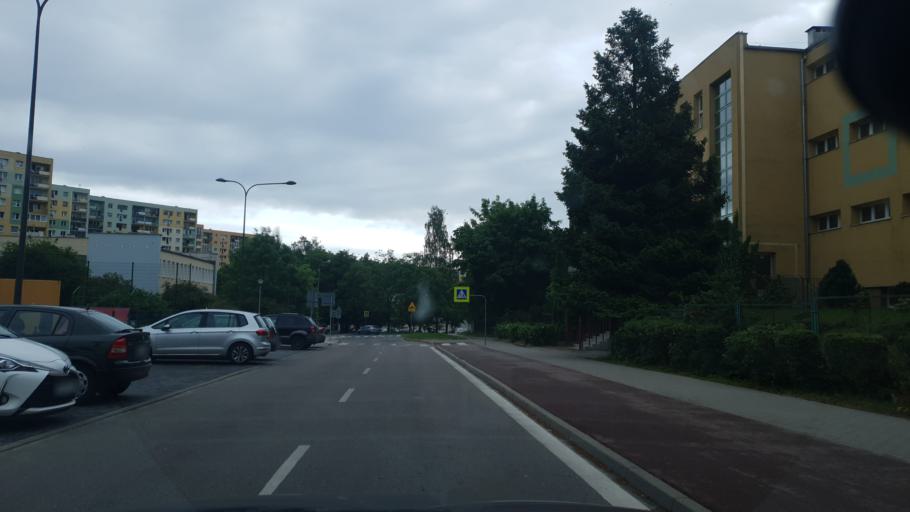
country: PL
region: Pomeranian Voivodeship
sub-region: Sopot
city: Sopot
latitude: 54.4571
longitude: 18.5320
